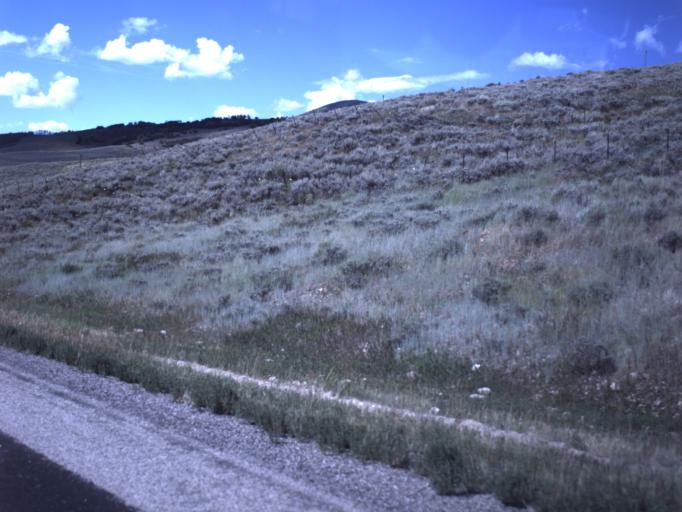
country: US
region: Utah
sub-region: Wasatch County
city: Heber
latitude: 40.2353
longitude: -111.1338
